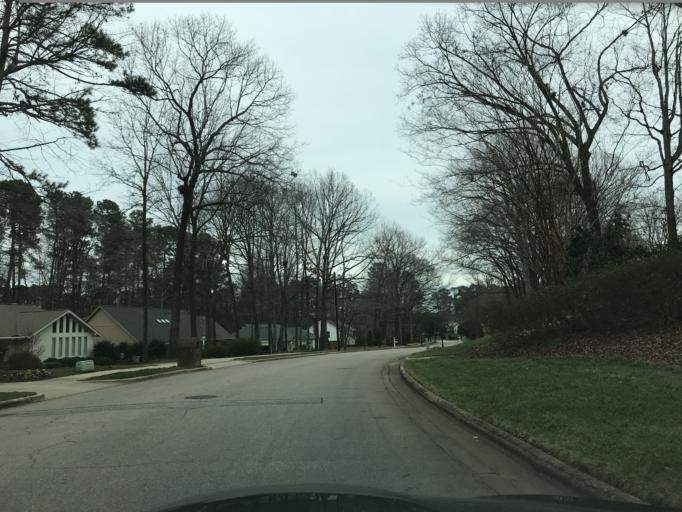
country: US
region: North Carolina
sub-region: Wake County
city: West Raleigh
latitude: 35.8778
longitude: -78.6116
